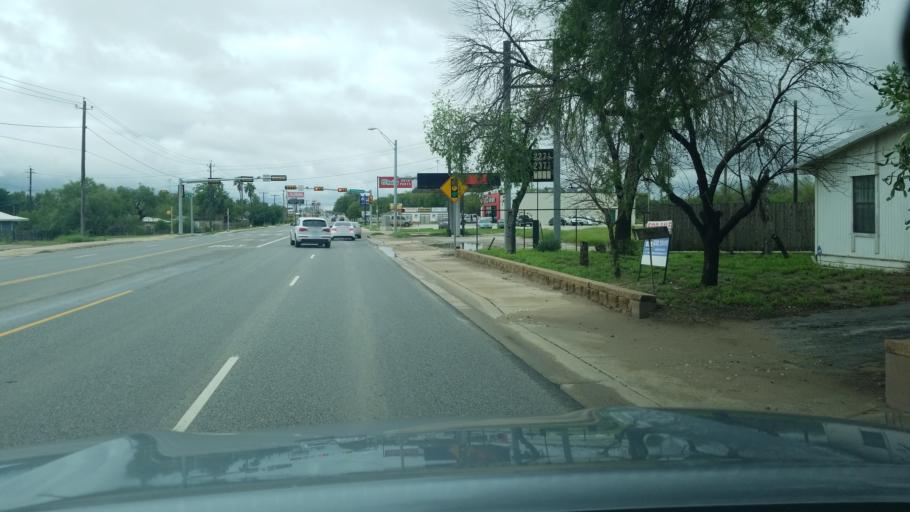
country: US
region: Texas
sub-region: Dimmit County
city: Carrizo Springs
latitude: 28.5289
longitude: -99.8540
